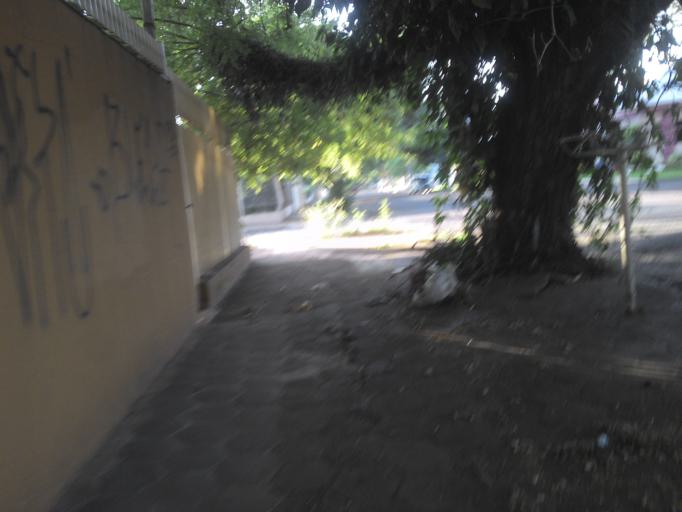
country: BR
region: Parana
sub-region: Maringa
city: Maringa
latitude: -23.4292
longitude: -51.9382
